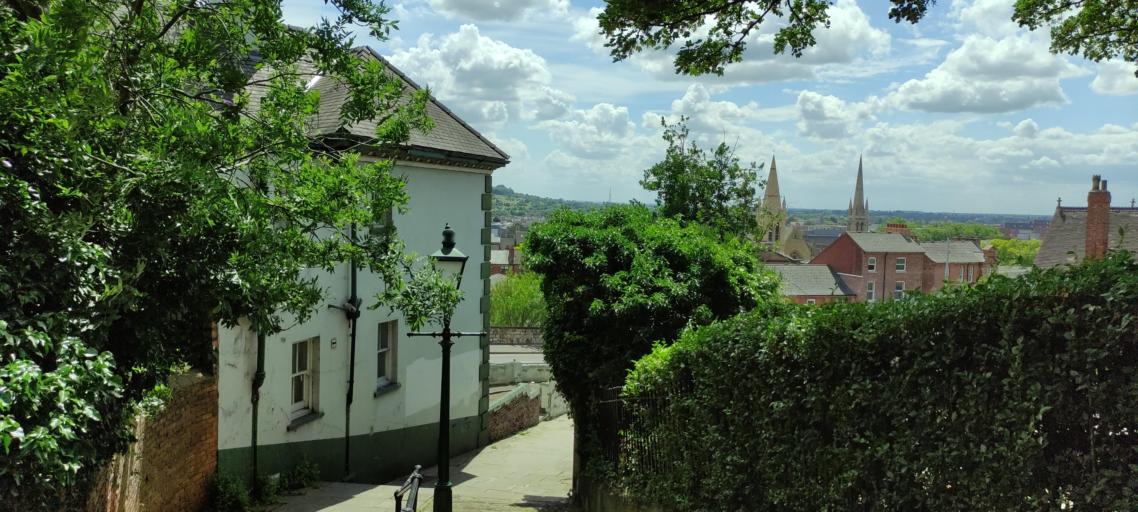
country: GB
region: England
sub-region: Lincolnshire
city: Lincoln
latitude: 53.2324
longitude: -0.5342
